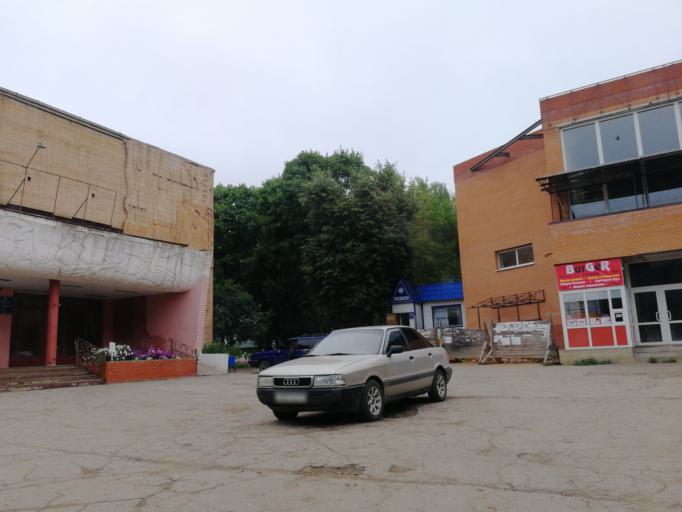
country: RU
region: Tula
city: Bogoroditsk
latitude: 53.7700
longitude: 38.1256
